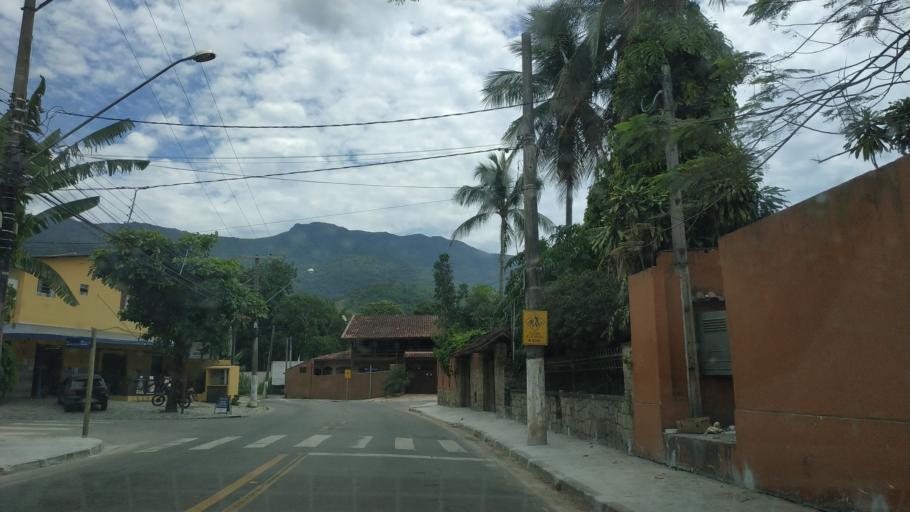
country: BR
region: Sao Paulo
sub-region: Ilhabela
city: Ilhabela
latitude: -23.8234
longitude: -45.3613
